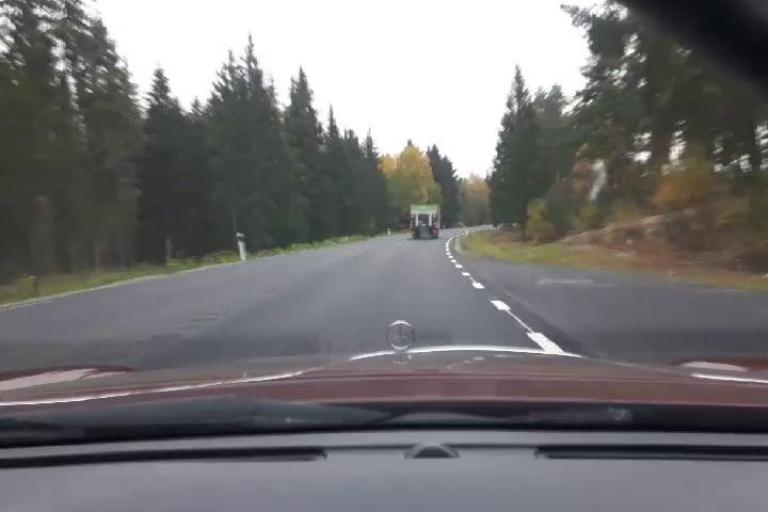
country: SE
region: Soedermanland
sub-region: Strangnas Kommun
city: Strangnas
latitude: 59.4177
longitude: 17.0205
